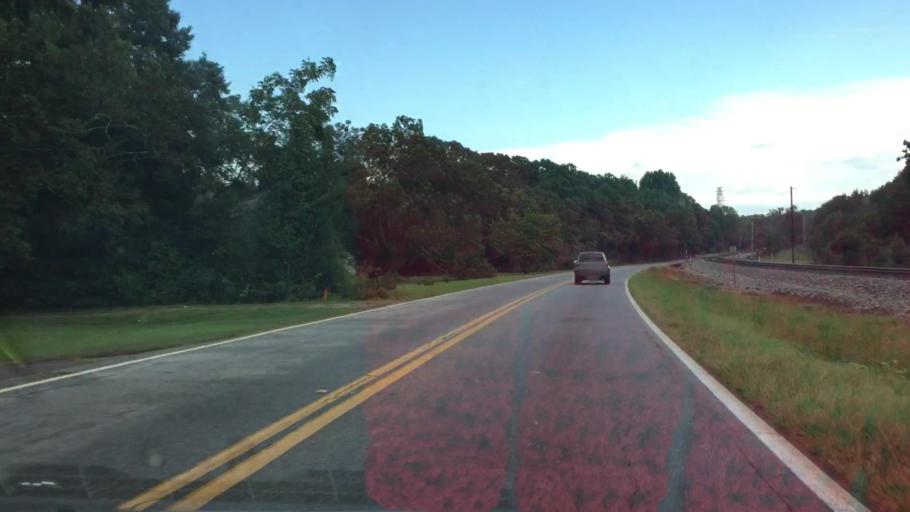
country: US
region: Georgia
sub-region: Clayton County
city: Lovejoy
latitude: 33.4315
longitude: -84.2914
